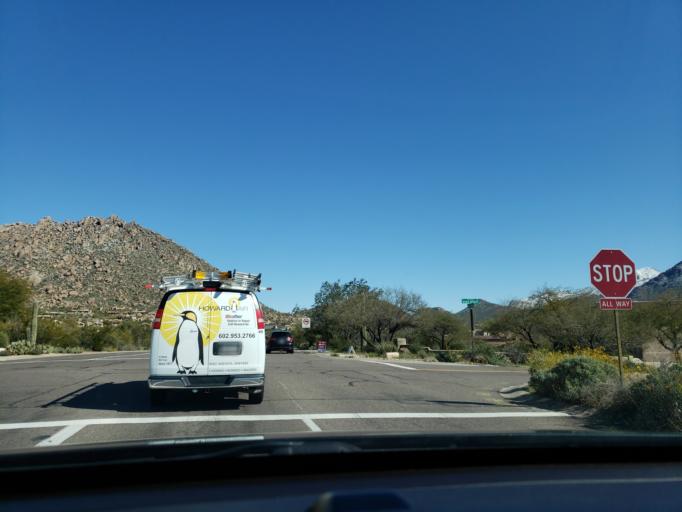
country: US
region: Arizona
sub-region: Maricopa County
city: Carefree
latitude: 33.7126
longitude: -111.8570
